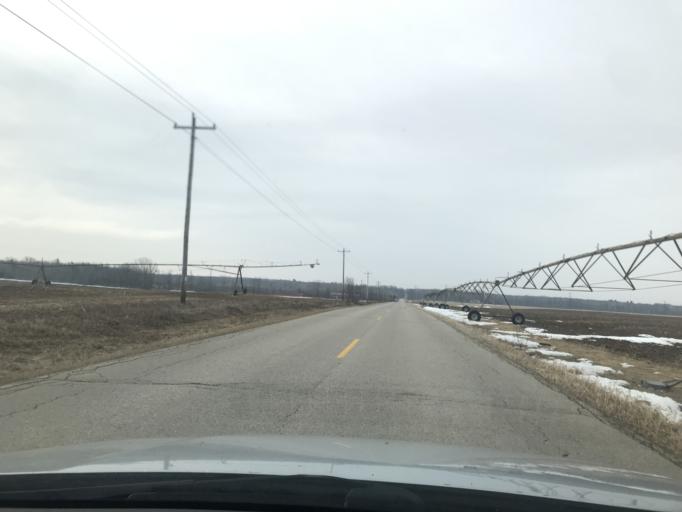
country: US
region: Wisconsin
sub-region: Oconto County
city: Oconto Falls
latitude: 44.8482
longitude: -88.1675
